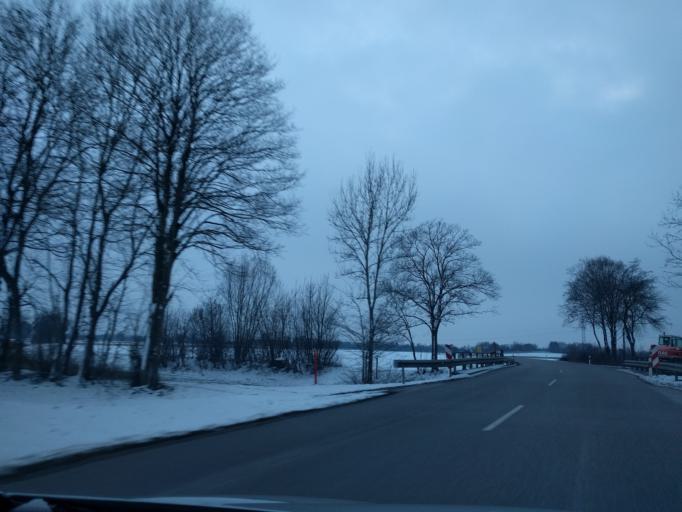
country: DE
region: Bavaria
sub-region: Swabia
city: Asbach-Baumenheim
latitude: 48.7064
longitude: 10.8157
